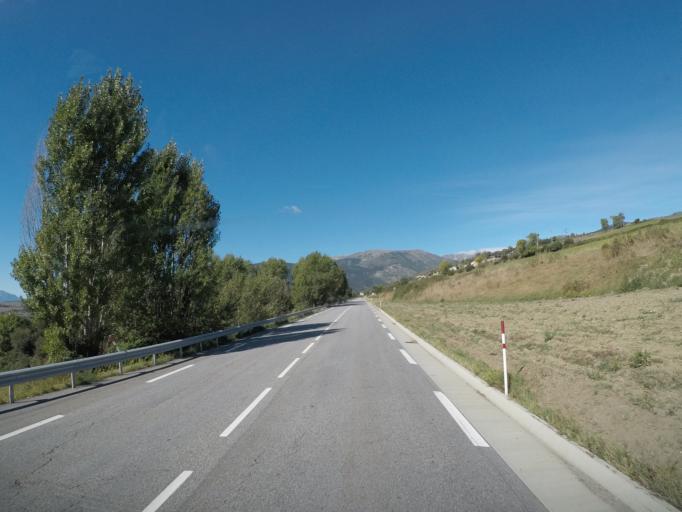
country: ES
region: Catalonia
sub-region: Provincia de Girona
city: Puigcerda
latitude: 42.4568
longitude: 1.9285
